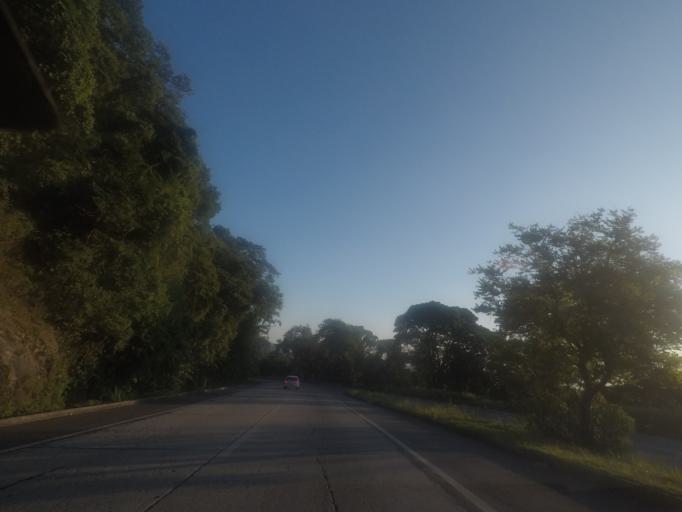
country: BR
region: Rio de Janeiro
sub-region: Petropolis
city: Petropolis
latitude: -22.5338
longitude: -43.2336
